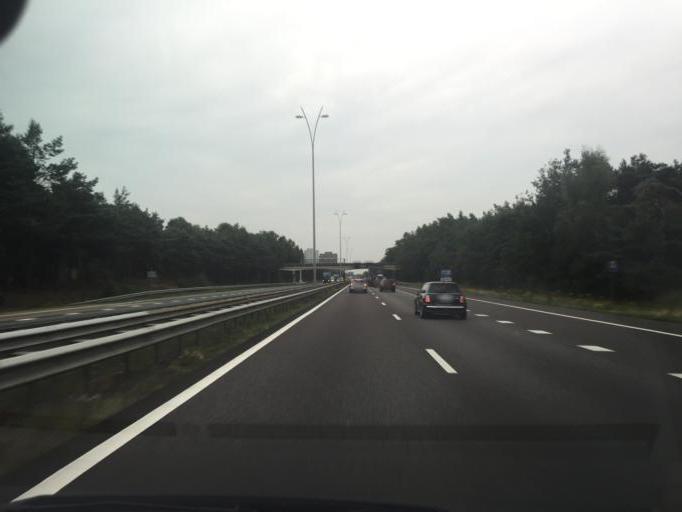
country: NL
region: North Brabant
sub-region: Gemeente Eindhoven
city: De Doornakkers
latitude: 51.4048
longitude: 5.5127
